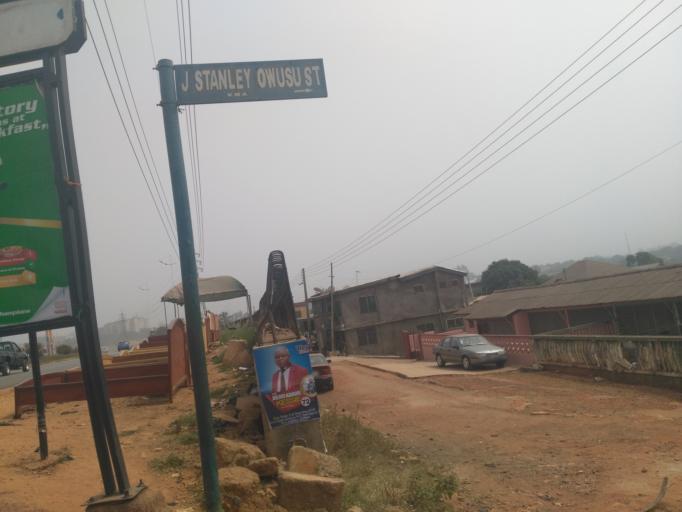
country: GH
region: Ashanti
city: Kumasi
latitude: 6.6978
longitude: -1.6404
